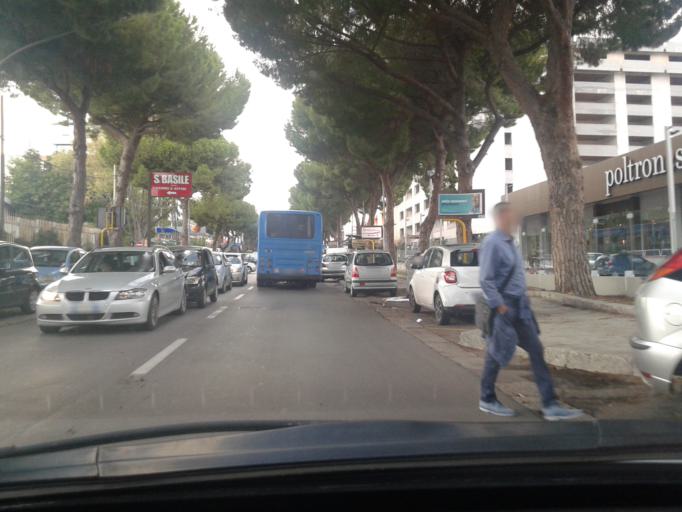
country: IT
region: Sicily
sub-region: Palermo
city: Palermo
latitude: 38.1573
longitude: 13.3181
